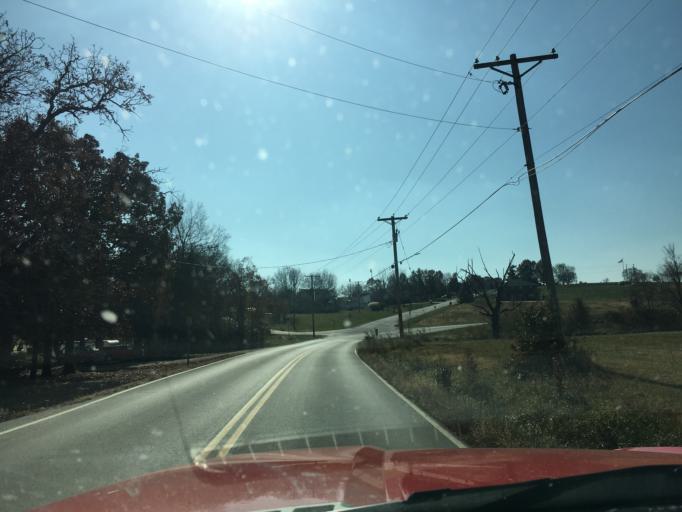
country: US
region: Missouri
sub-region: Cole County
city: Wardsville
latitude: 38.5001
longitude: -92.1762
